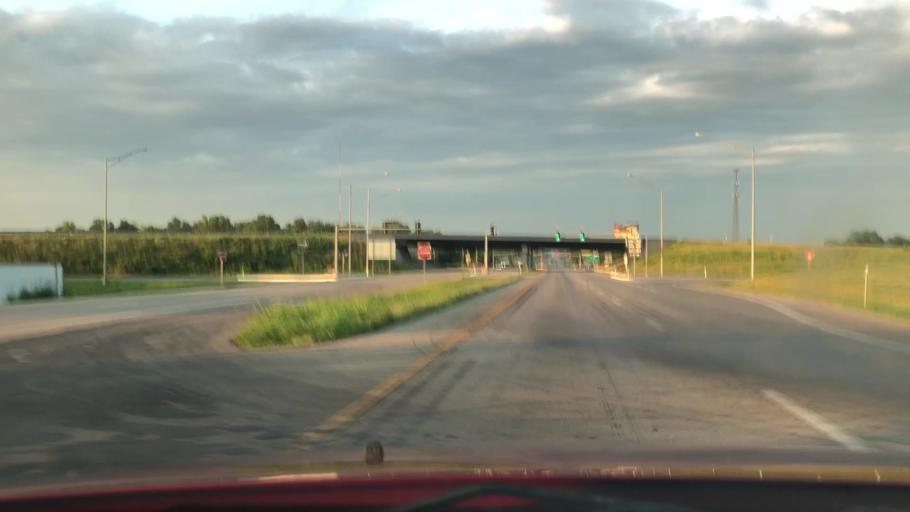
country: US
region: Missouri
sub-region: Greene County
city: Battlefield
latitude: 37.1604
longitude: -93.4010
